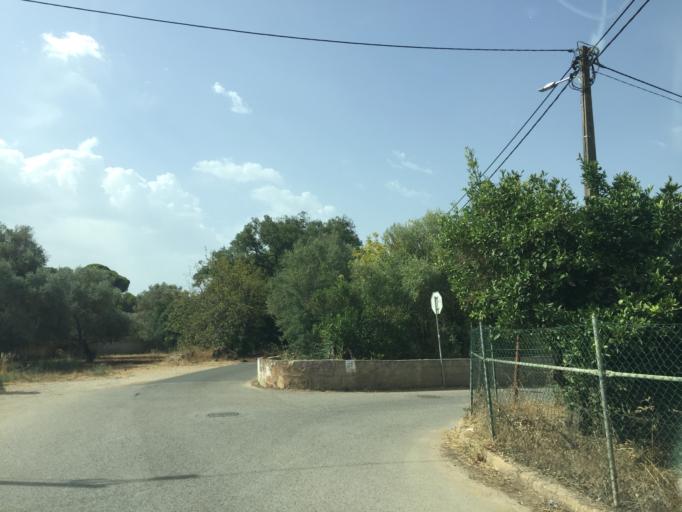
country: PT
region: Faro
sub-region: Loule
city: Vilamoura
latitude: 37.1054
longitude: -8.1060
